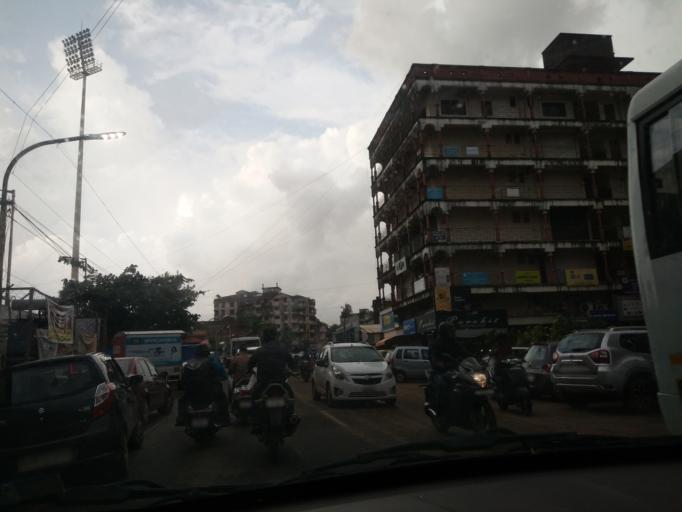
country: IN
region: Goa
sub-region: South Goa
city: Madgaon
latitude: 15.2892
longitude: 73.9633
